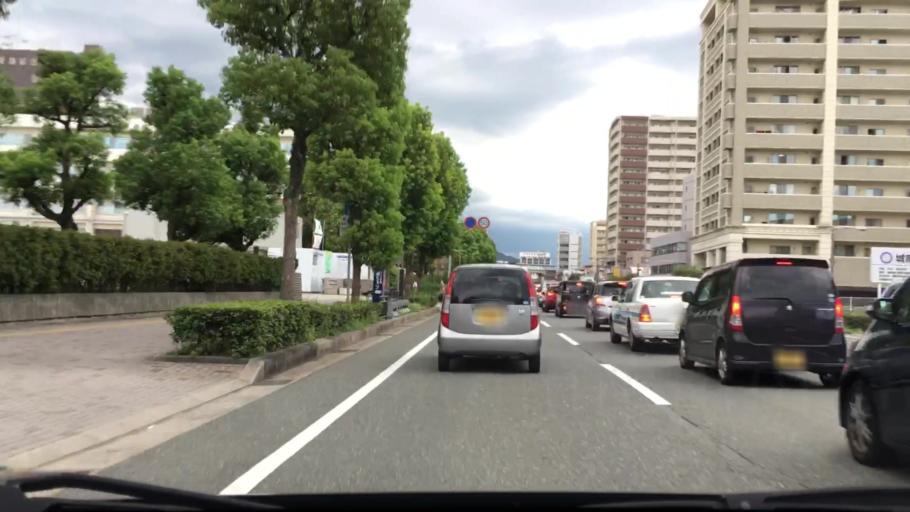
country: JP
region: Hyogo
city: Himeji
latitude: 34.8215
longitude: 134.6928
